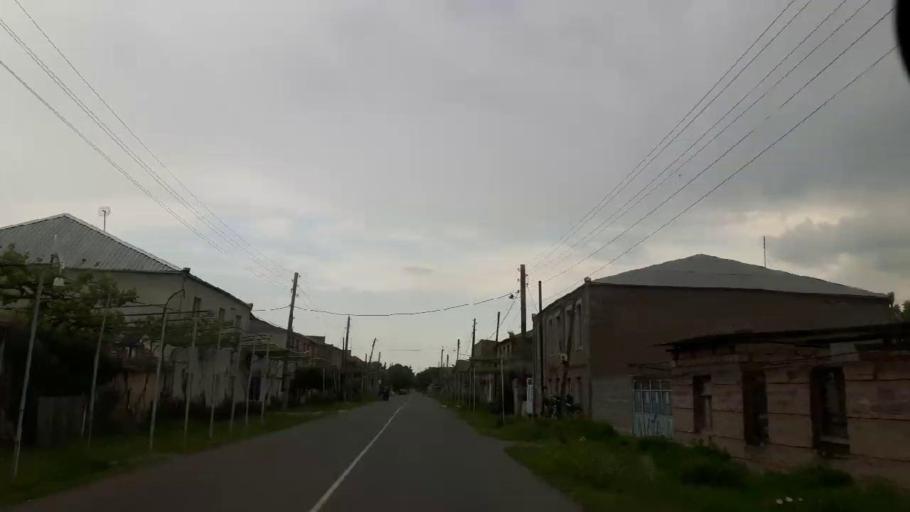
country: GE
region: Shida Kartli
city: Gori
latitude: 41.9615
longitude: 44.2030
